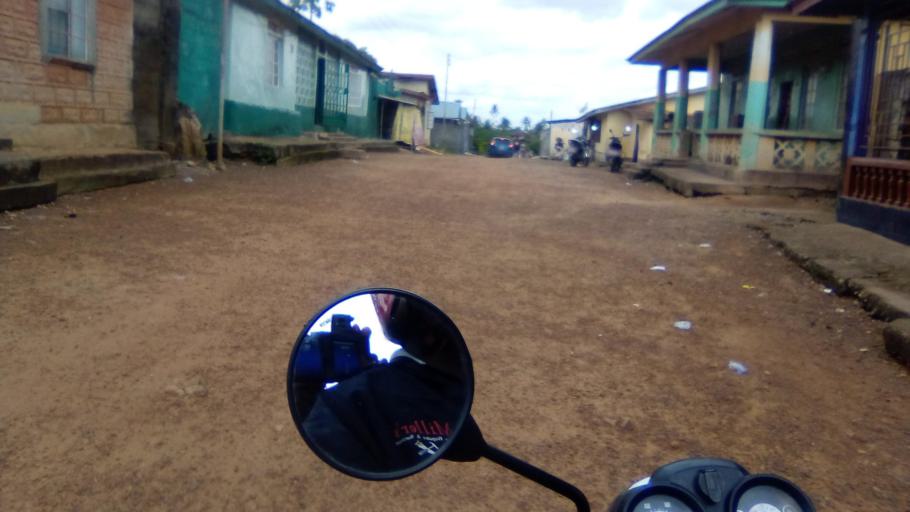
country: SL
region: Southern Province
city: Bo
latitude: 7.9621
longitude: -11.7323
